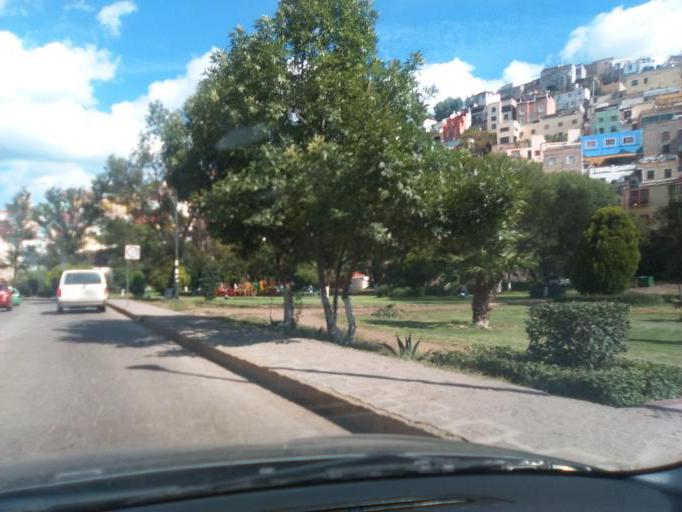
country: MX
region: Guanajuato
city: Guanajuato
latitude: 21.0160
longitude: -101.2650
